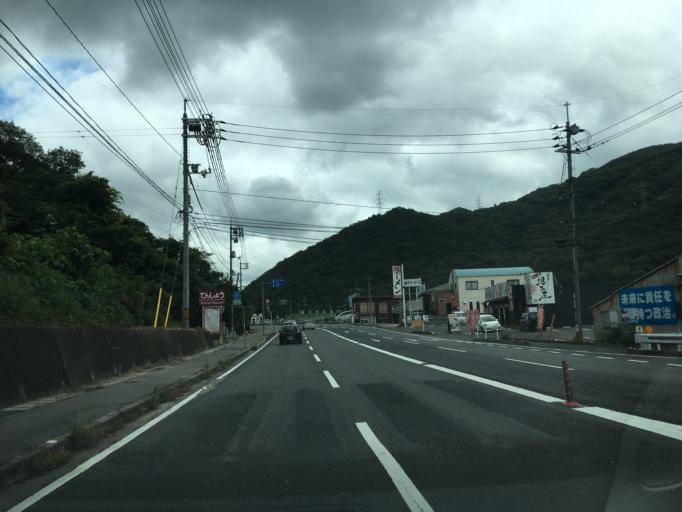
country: JP
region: Okayama
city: Okayama-shi
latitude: 34.7264
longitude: 133.9831
